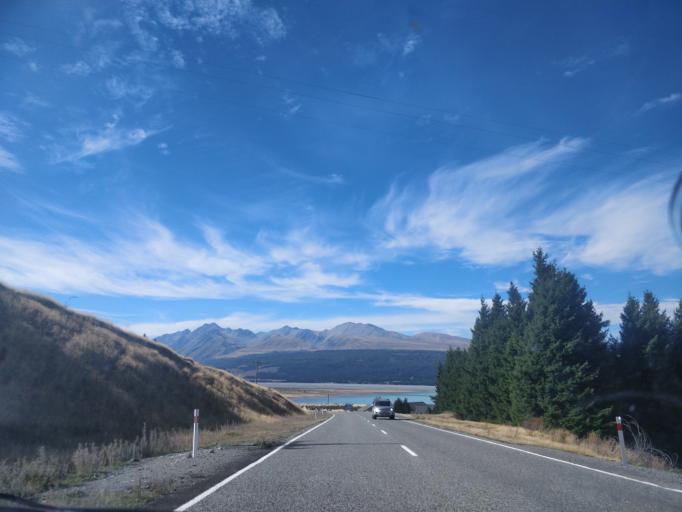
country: NZ
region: Canterbury
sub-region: Timaru District
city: Pleasant Point
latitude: -43.9131
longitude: 170.1181
